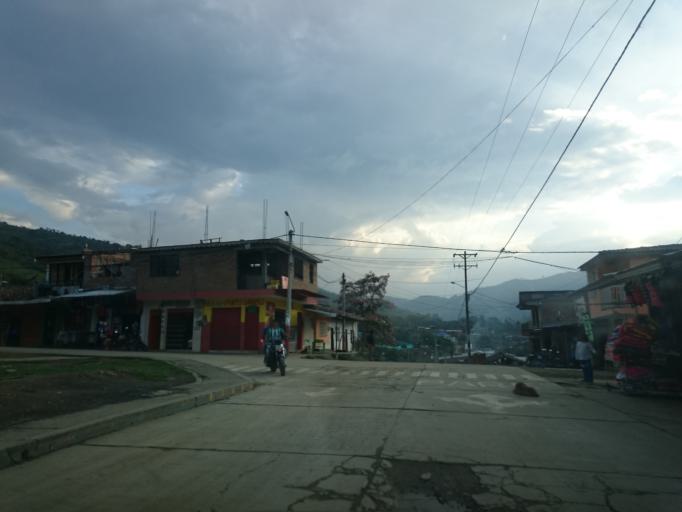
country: CO
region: Cauca
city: Toribio
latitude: 2.9558
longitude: -76.2690
